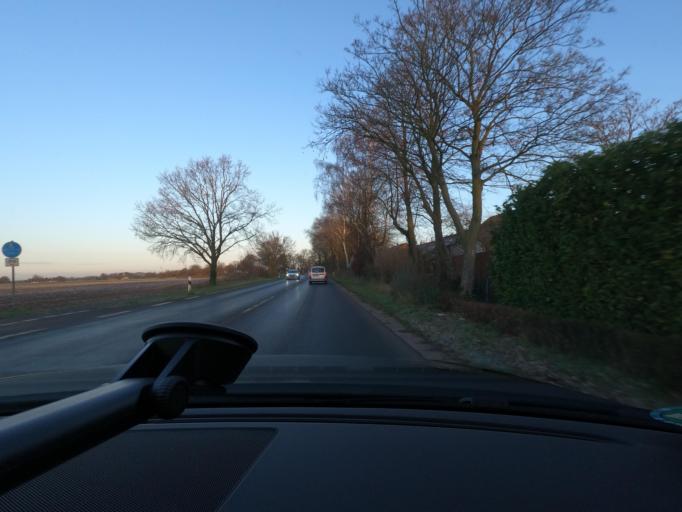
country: DE
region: North Rhine-Westphalia
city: Kempen
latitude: 51.3739
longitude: 6.4028
